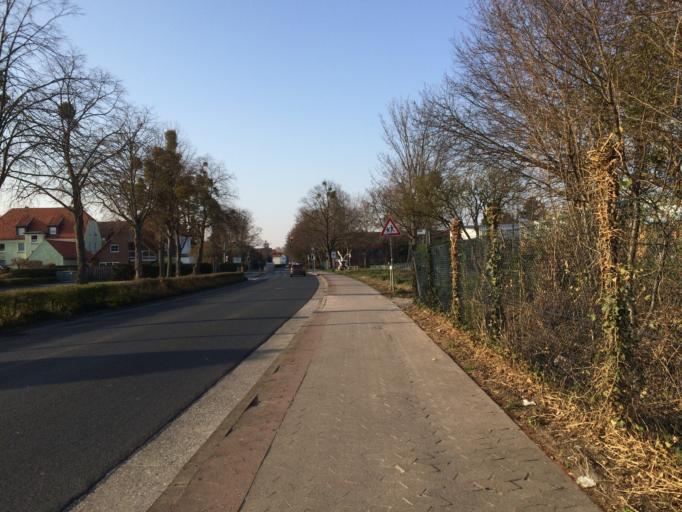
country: DE
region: Lower Saxony
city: Gehrden
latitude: 52.3104
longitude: 9.6075
